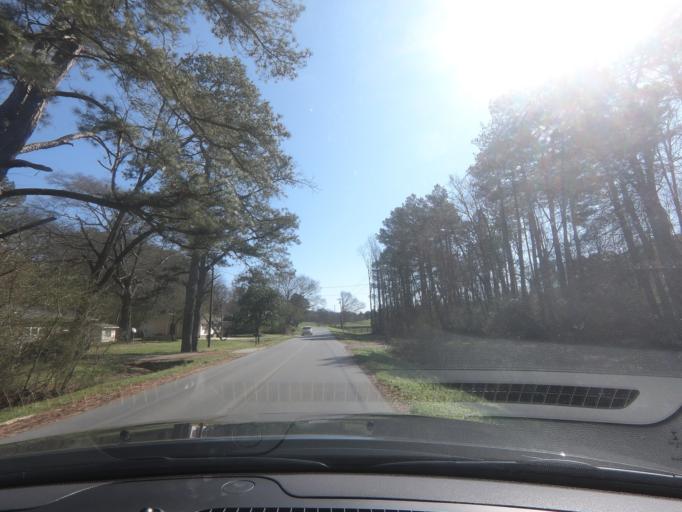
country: US
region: Georgia
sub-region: Gordon County
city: Calhoun
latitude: 34.4619
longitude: -84.9987
